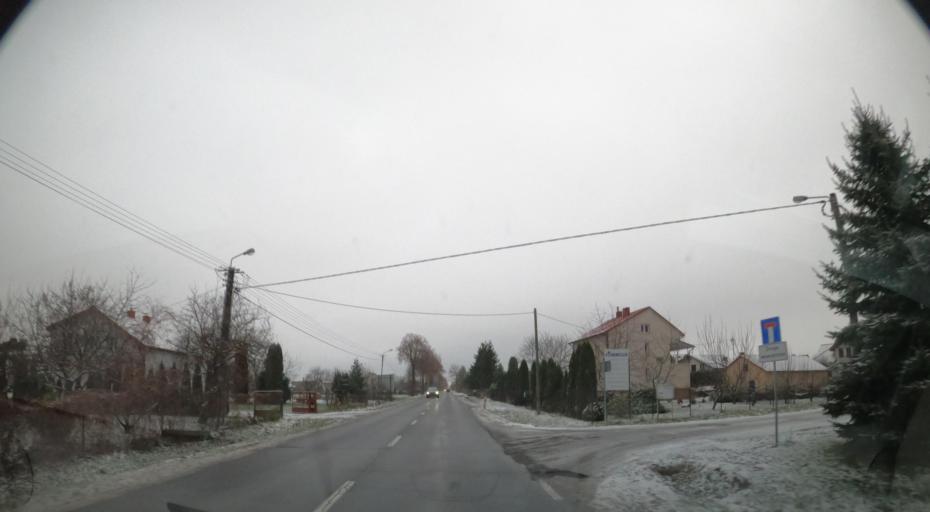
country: PL
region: Masovian Voivodeship
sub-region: Powiat plocki
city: Maszewo Duze
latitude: 52.5636
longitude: 19.6333
